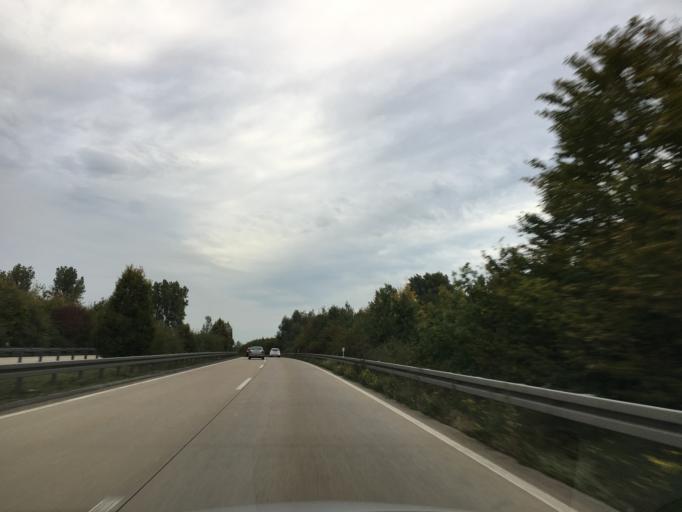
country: DE
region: North Rhine-Westphalia
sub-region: Regierungsbezirk Dusseldorf
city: Ratingen
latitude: 51.3022
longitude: 6.7735
